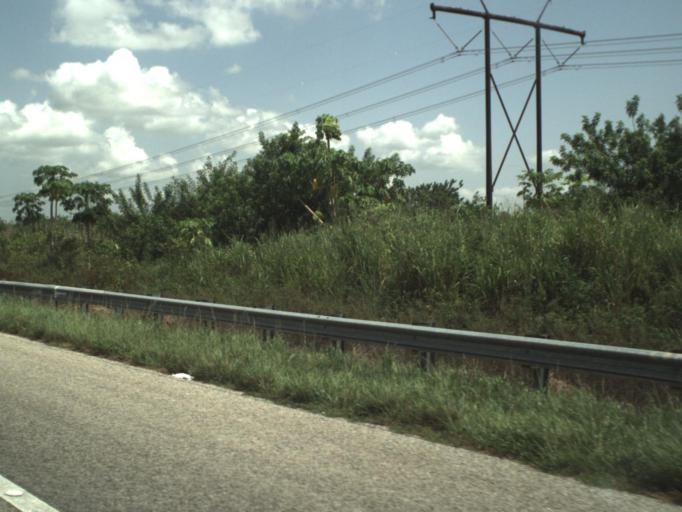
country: US
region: Florida
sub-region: Broward County
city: Weston
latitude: 26.2561
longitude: -80.4768
